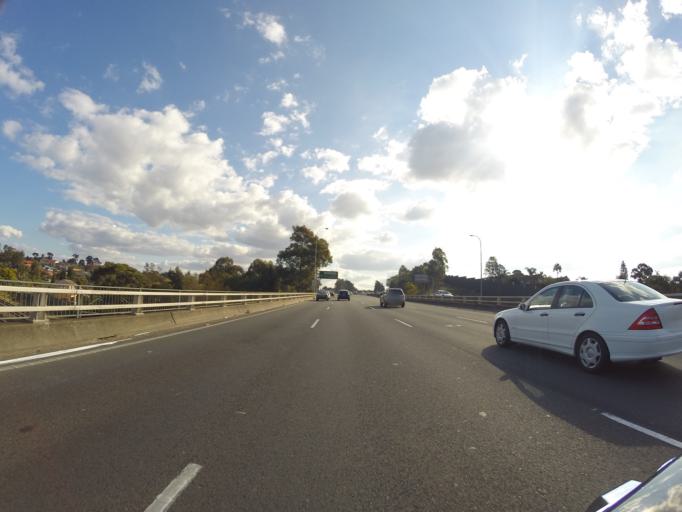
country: AU
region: New South Wales
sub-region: Campbelltown Municipality
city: Glenfield
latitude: -33.9390
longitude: 150.9184
